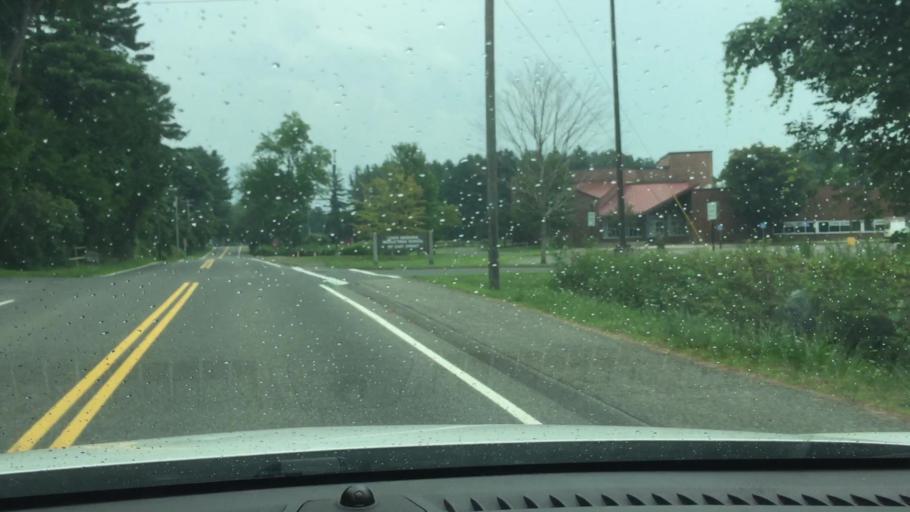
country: US
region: Massachusetts
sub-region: Berkshire County
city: Lenox
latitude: 42.3529
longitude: -73.2582
